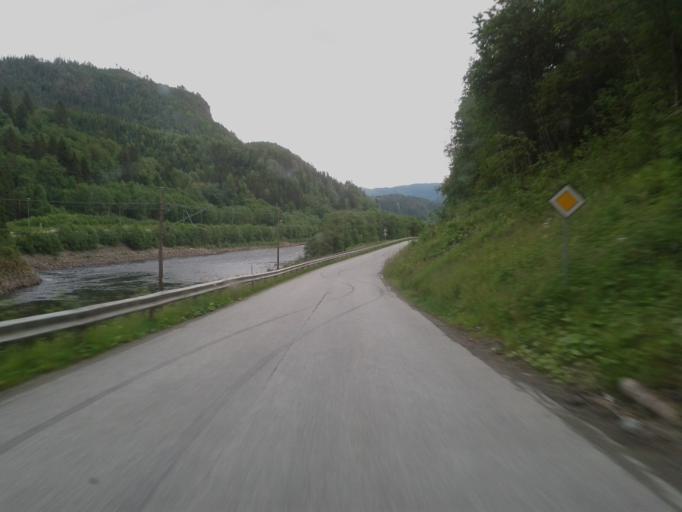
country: NO
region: Sor-Trondelag
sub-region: Midtre Gauldal
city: Storen
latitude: 63.0652
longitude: 10.2865
